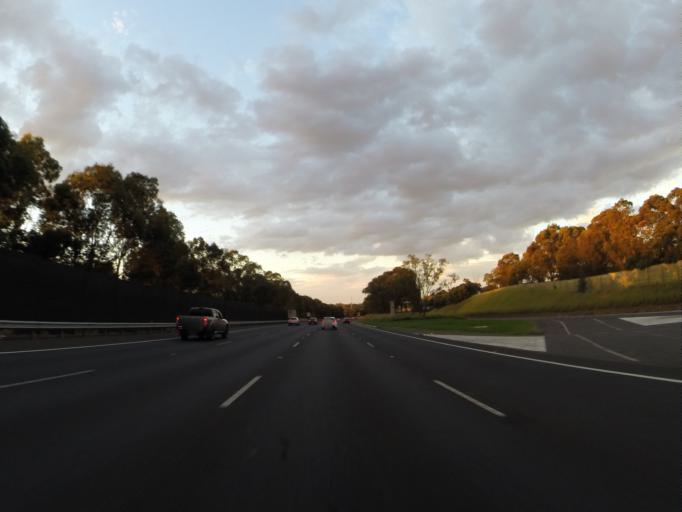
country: AU
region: New South Wales
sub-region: Campbelltown Municipality
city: Leumeah
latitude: -34.0179
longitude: 150.8249
